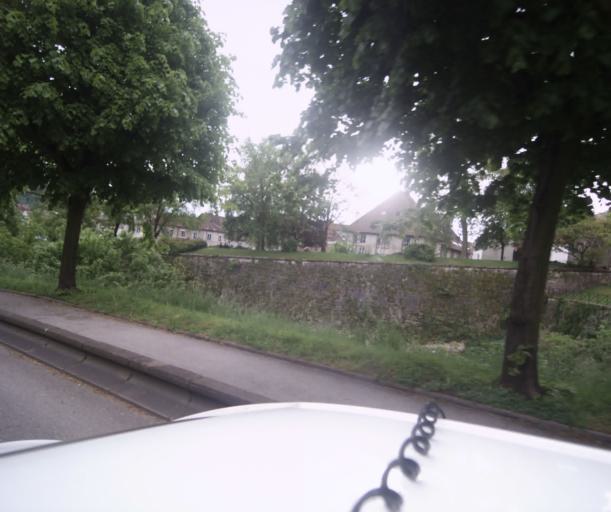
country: FR
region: Franche-Comte
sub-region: Departement du Doubs
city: Besancon
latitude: 47.2438
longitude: 6.0233
